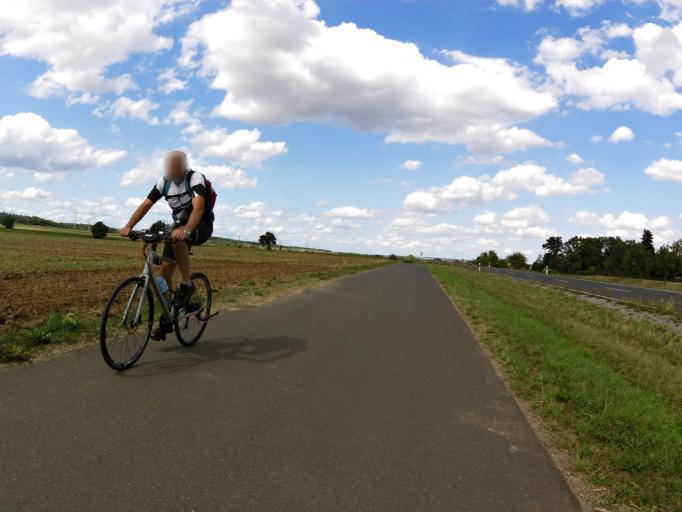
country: DE
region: Bavaria
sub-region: Regierungsbezirk Unterfranken
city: Bergrheinfeld
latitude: 49.9915
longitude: 10.1700
